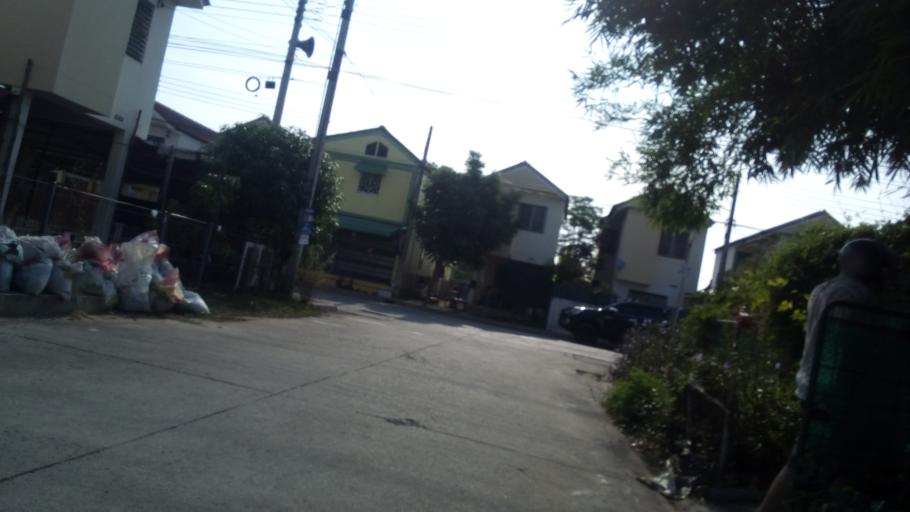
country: TH
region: Pathum Thani
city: Nong Suea
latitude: 14.0529
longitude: 100.8391
